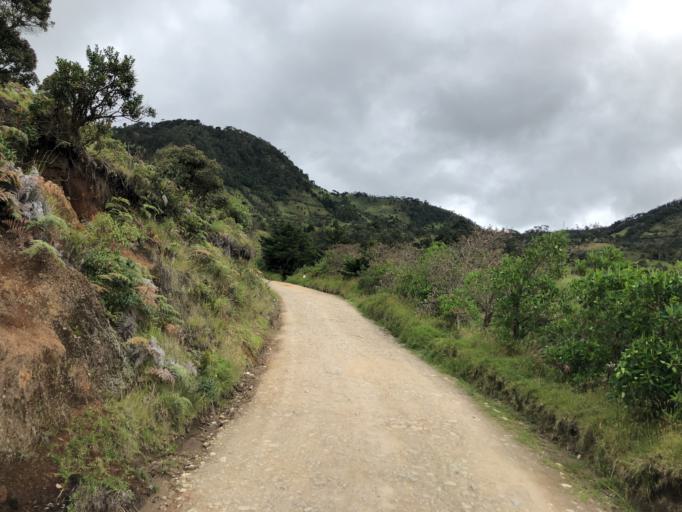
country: CO
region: Cauca
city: Totoro
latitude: 2.5099
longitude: -76.3666
